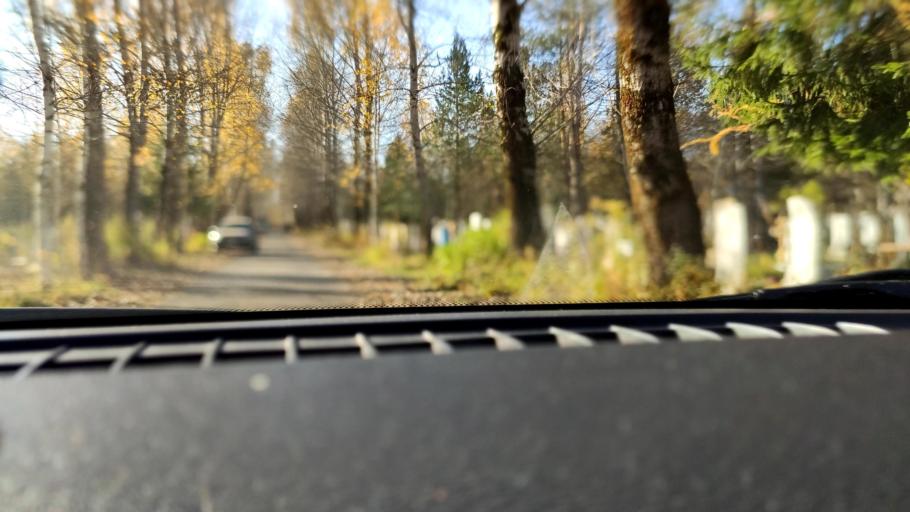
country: RU
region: Perm
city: Kondratovo
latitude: 58.0668
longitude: 56.1372
